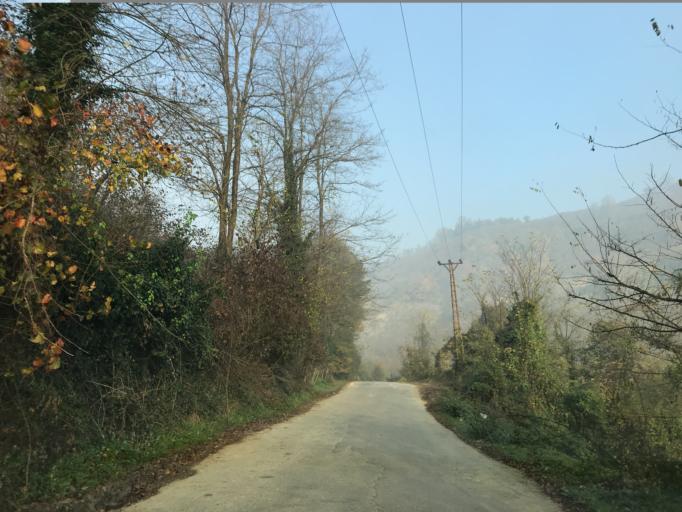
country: TR
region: Duzce
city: Cumayeri
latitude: 40.9151
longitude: 30.9357
